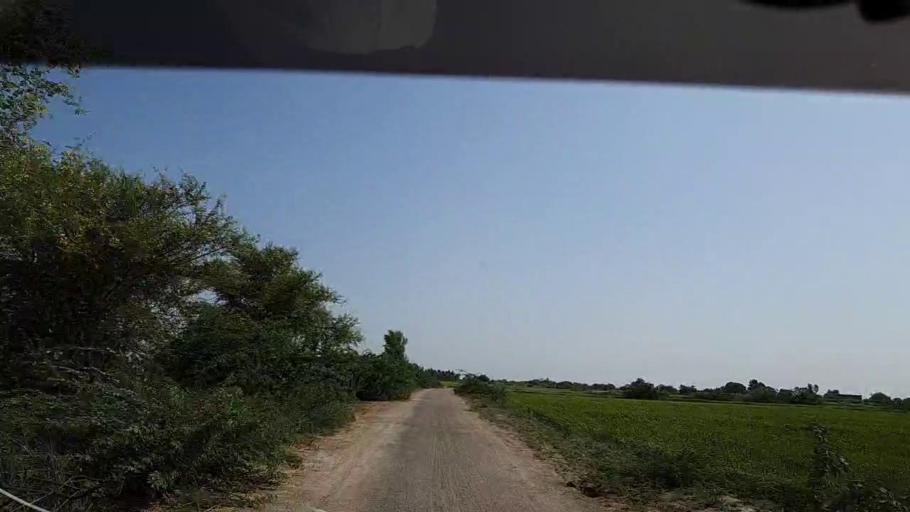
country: PK
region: Sindh
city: Badin
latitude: 24.6272
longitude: 68.7826
